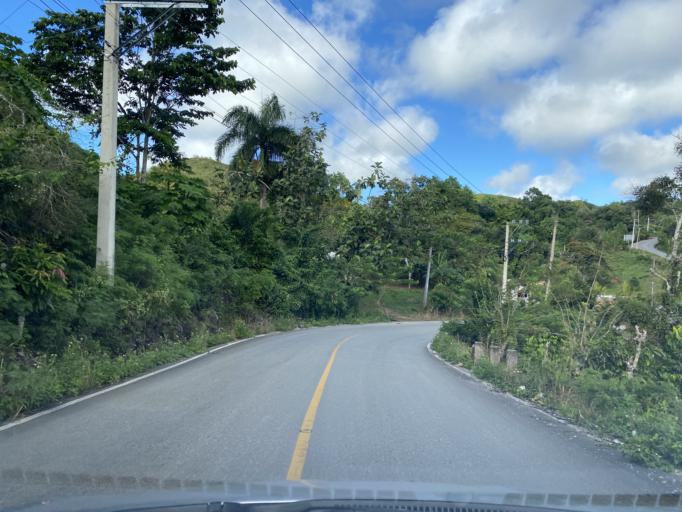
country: DO
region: Samana
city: Las Terrenas
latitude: 19.2684
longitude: -69.5606
